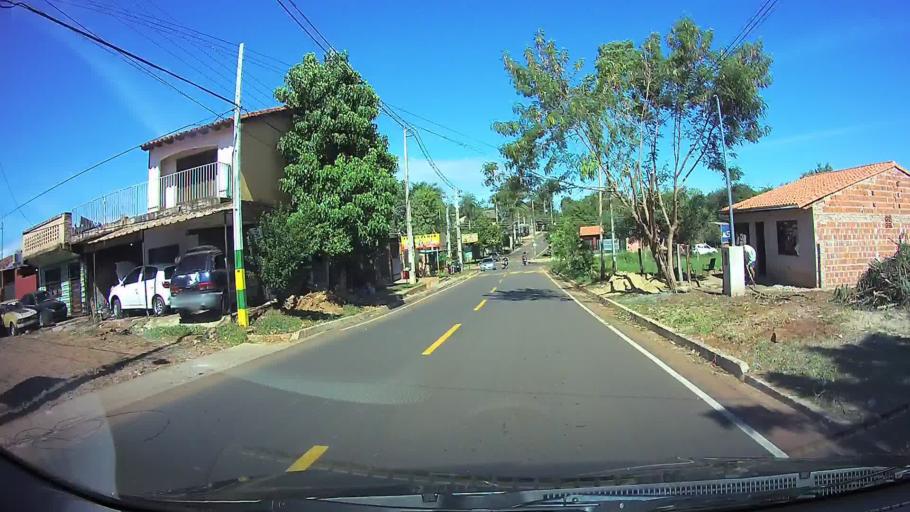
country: PY
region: Central
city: San Lorenzo
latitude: -25.2663
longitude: -57.4706
